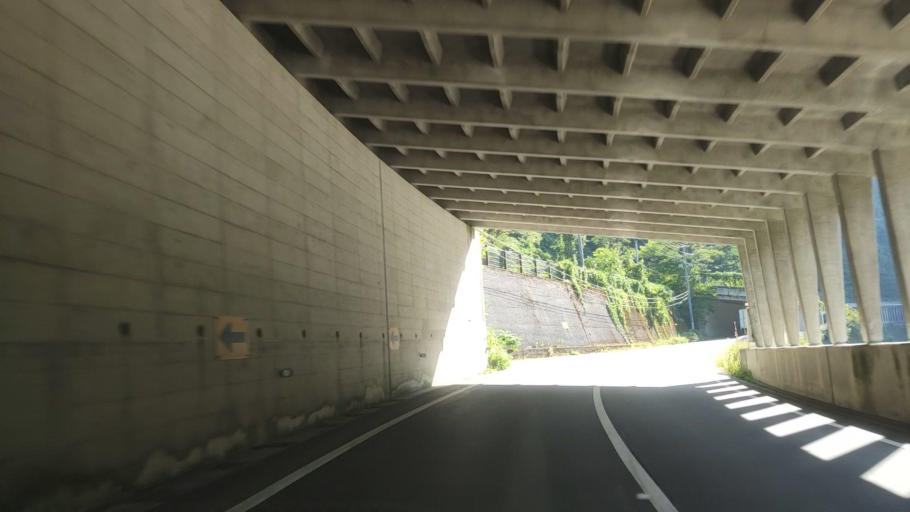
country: JP
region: Gifu
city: Takayama
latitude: 36.3125
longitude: 137.1305
